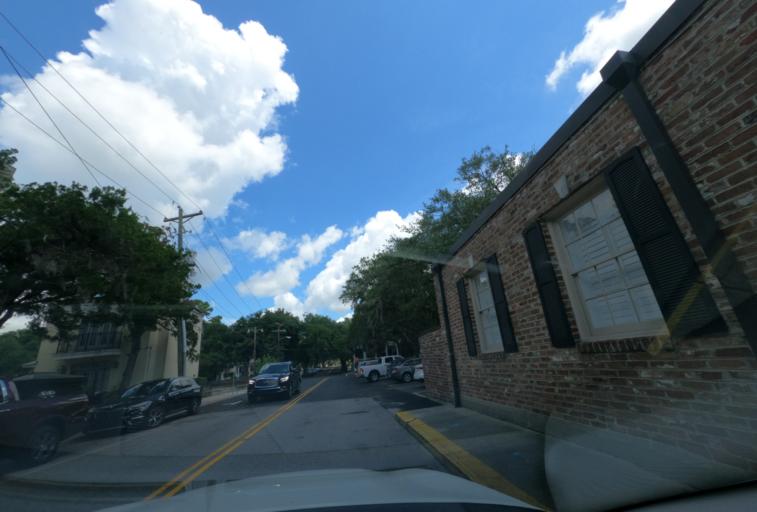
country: US
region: South Carolina
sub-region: Beaufort County
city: Beaufort
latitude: 32.4321
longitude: -80.6740
